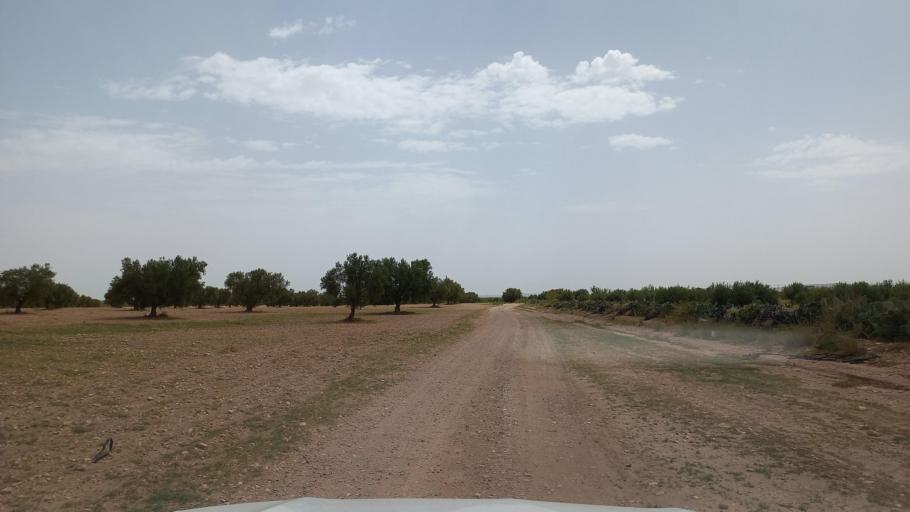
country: TN
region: Al Qasrayn
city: Kasserine
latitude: 35.2930
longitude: 9.0193
